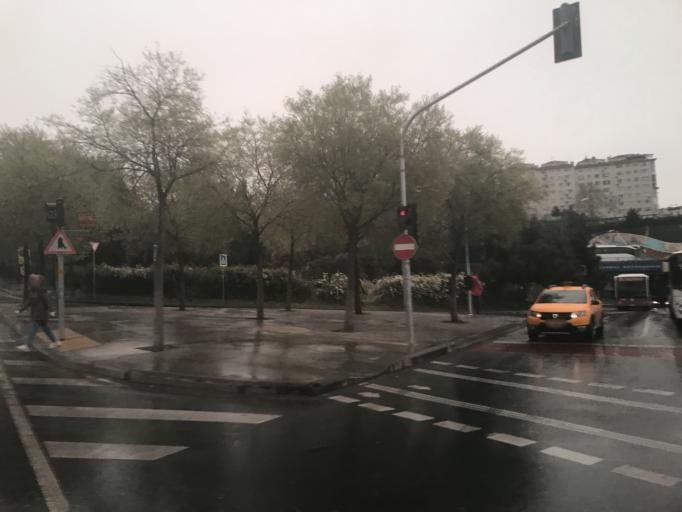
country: TR
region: Istanbul
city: Istanbul
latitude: 41.0489
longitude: 28.9446
